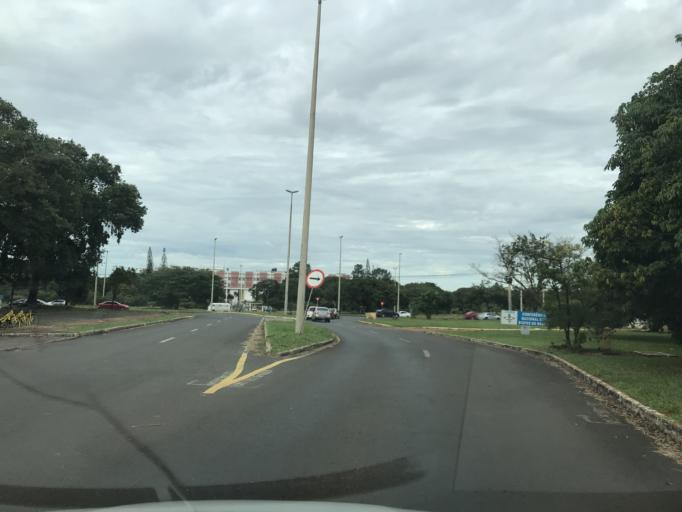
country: BR
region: Federal District
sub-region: Brasilia
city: Brasilia
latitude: -15.8020
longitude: -47.8746
